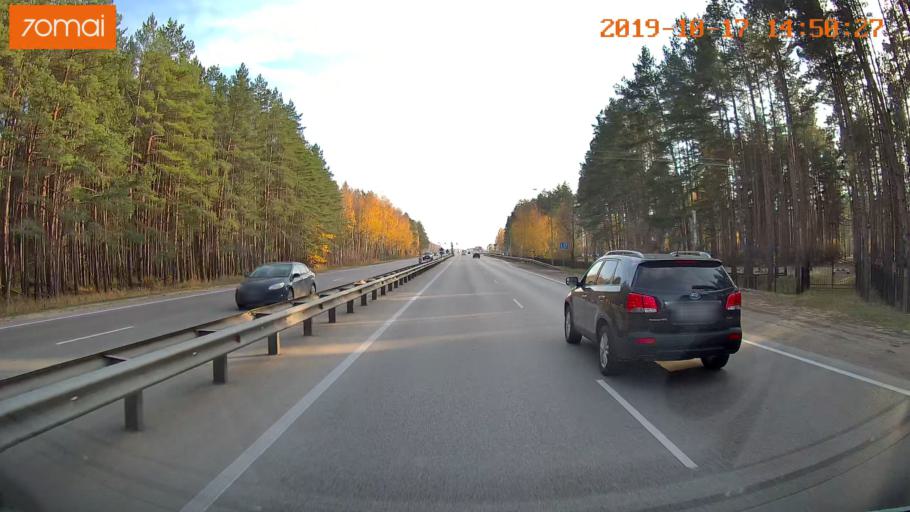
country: RU
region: Rjazan
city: Polyany
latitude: 54.7336
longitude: 39.8424
